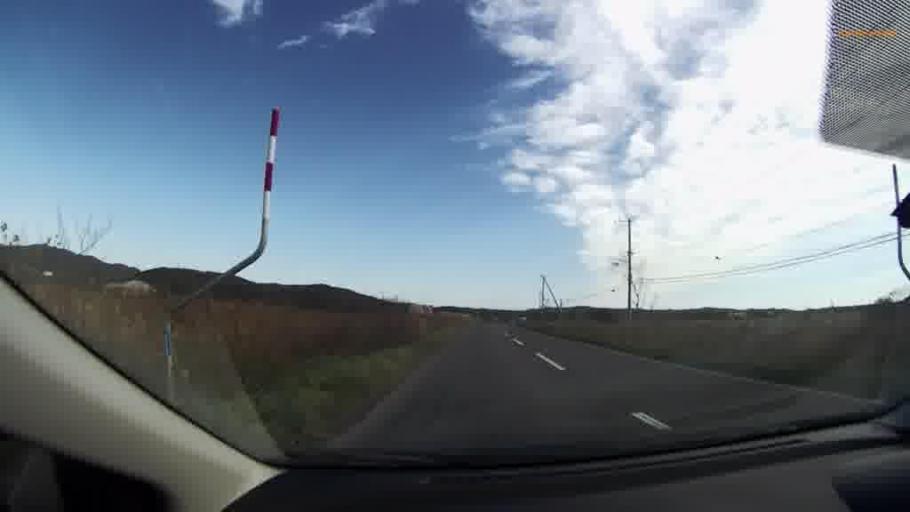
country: JP
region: Hokkaido
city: Kushiro
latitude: 42.9461
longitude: 144.0364
